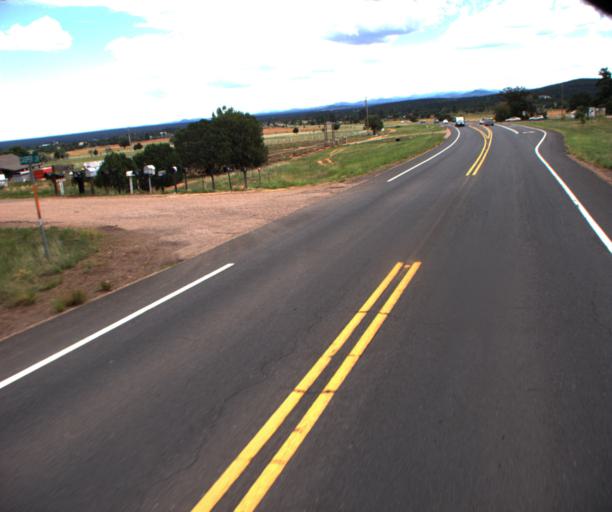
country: US
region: Arizona
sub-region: Navajo County
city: Linden
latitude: 34.2867
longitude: -110.1709
